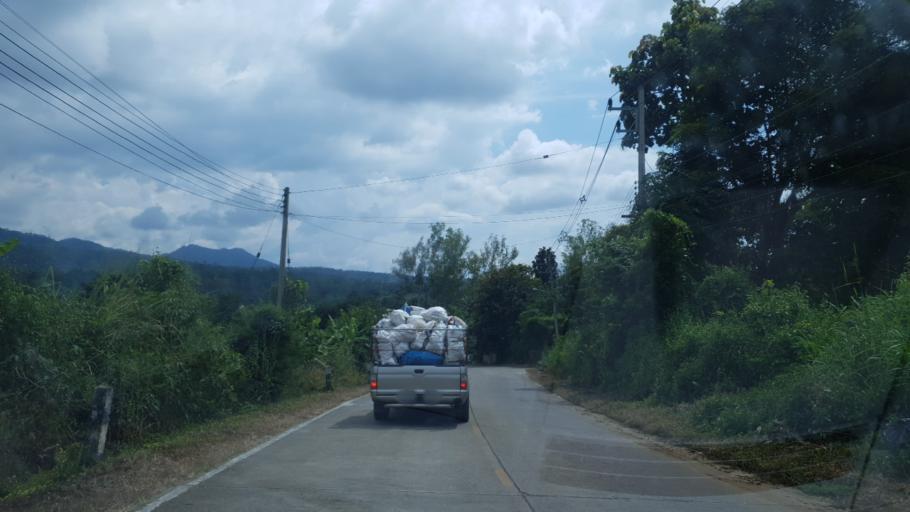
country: TH
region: Mae Hong Son
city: Khun Yuam
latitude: 18.8154
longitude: 97.9338
